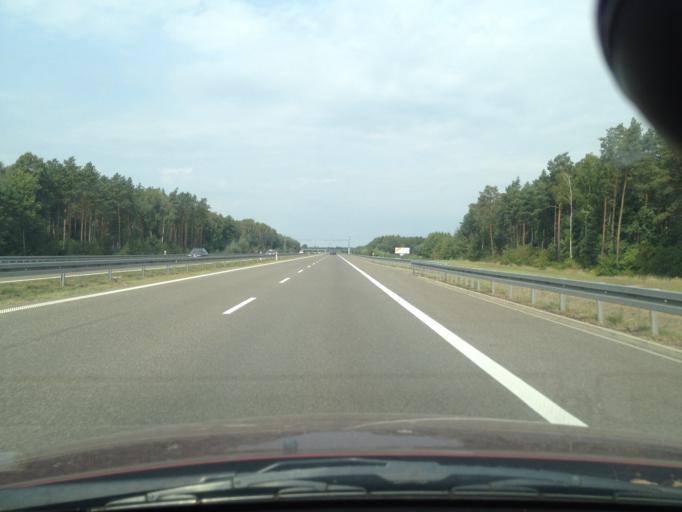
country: PL
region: West Pomeranian Voivodeship
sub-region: Powiat mysliborski
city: Nowogrodek Pomorski
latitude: 52.9324
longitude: 14.9842
